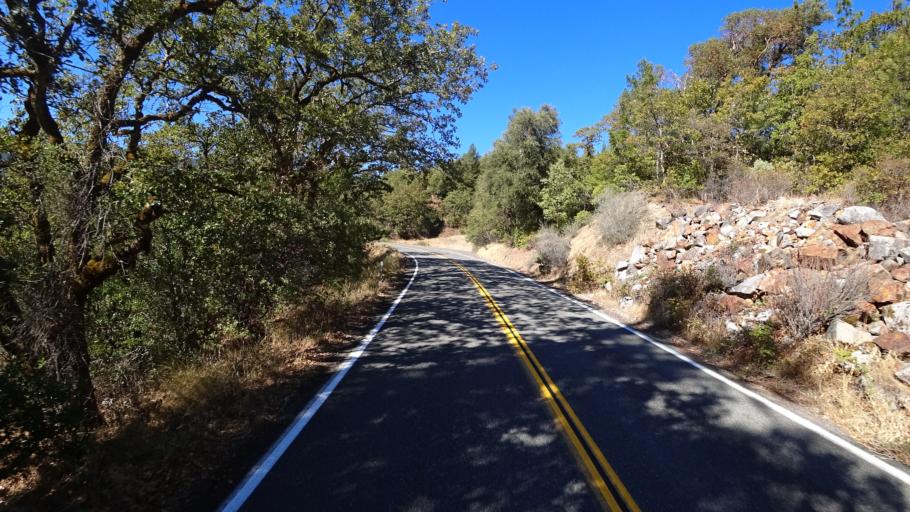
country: US
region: California
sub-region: Siskiyou County
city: Happy Camp
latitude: 41.3787
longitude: -123.4807
